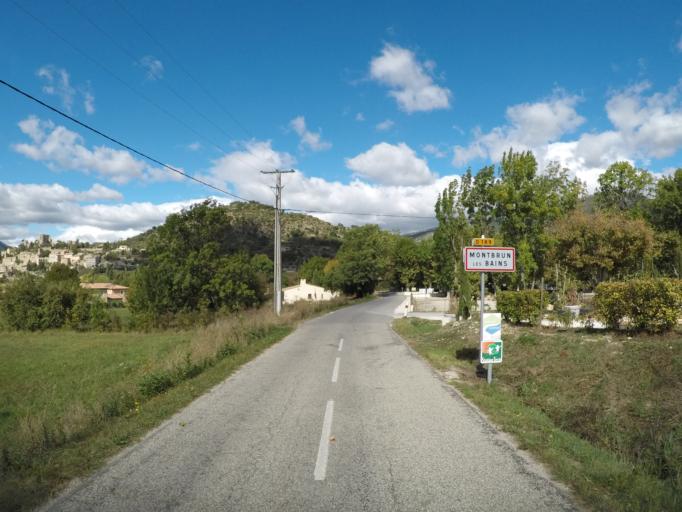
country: FR
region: Provence-Alpes-Cote d'Azur
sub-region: Departement du Vaucluse
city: Sault
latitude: 44.1717
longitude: 5.4460
